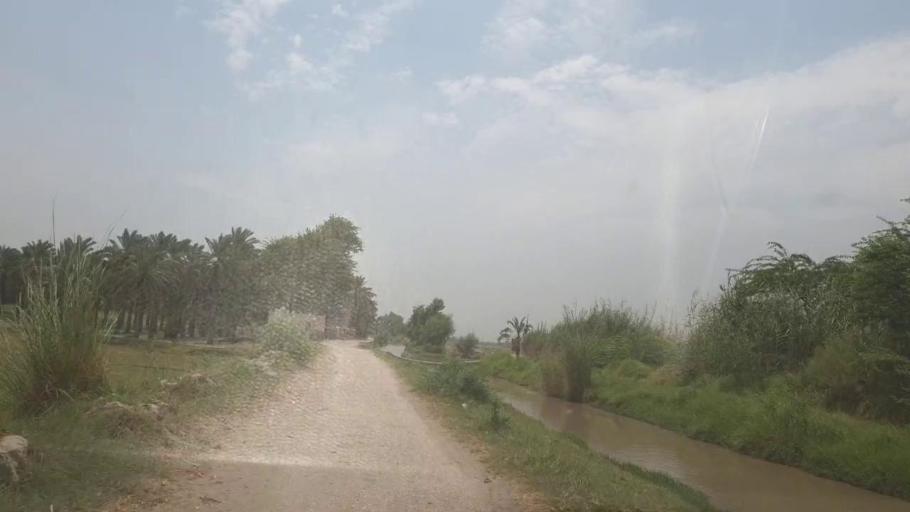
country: PK
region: Sindh
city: Kot Diji
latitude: 27.4435
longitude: 68.6760
